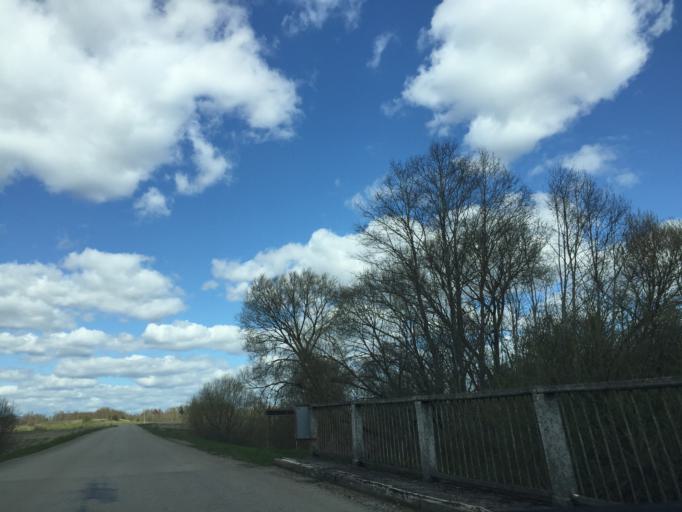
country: LV
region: Rezekne
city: Rezekne
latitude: 56.5486
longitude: 27.1503
